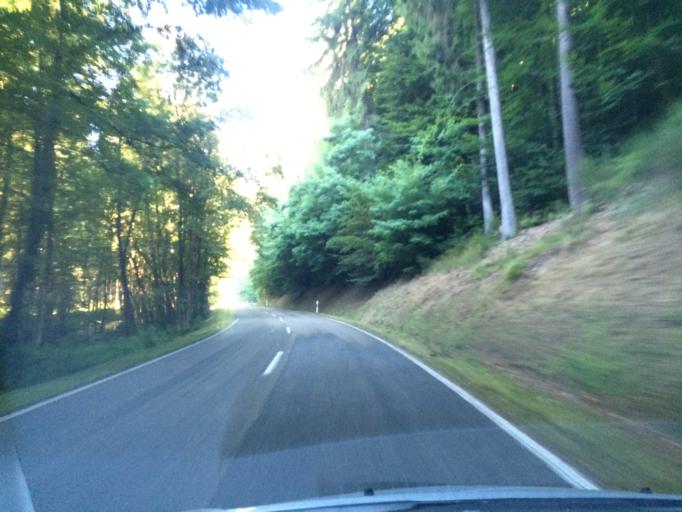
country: DE
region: Rheinland-Pfalz
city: Bobenthal
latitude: 49.0518
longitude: 7.8782
